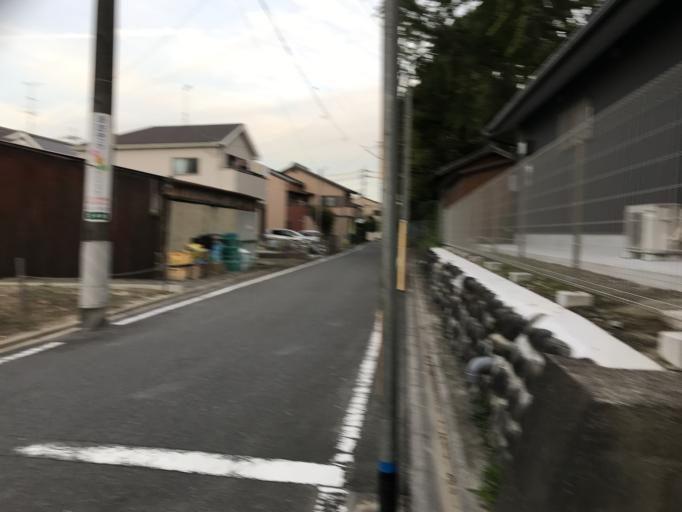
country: JP
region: Aichi
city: Nagoya-shi
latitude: 35.1924
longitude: 136.8514
